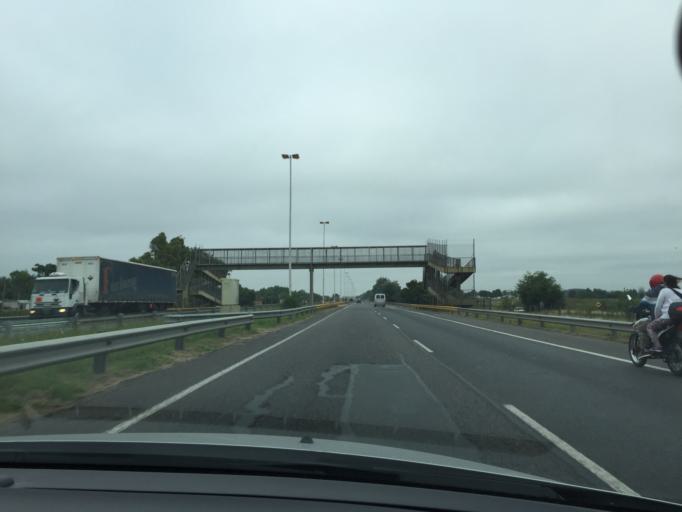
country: AR
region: Buenos Aires
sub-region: Partido de Ezeiza
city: Ezeiza
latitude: -34.8416
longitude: -58.5281
